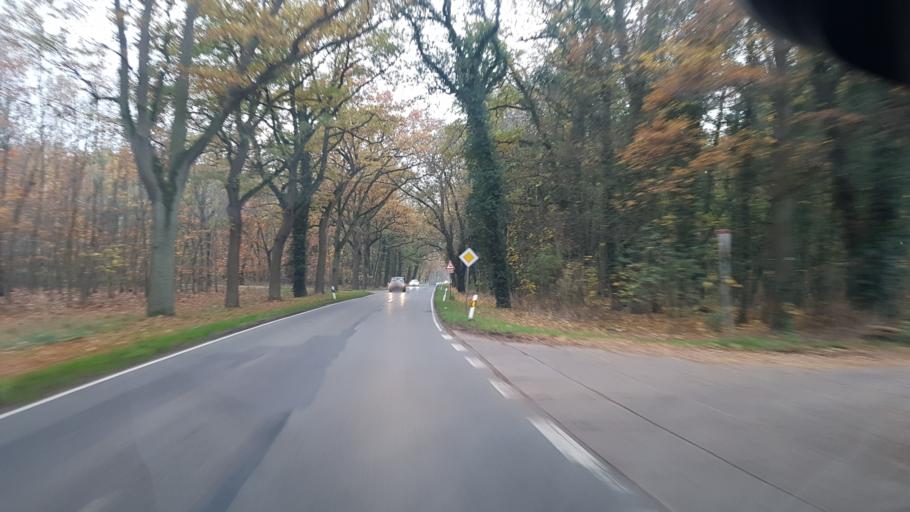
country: DE
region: Brandenburg
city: Fehrbellin
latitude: 52.8438
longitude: 12.8499
